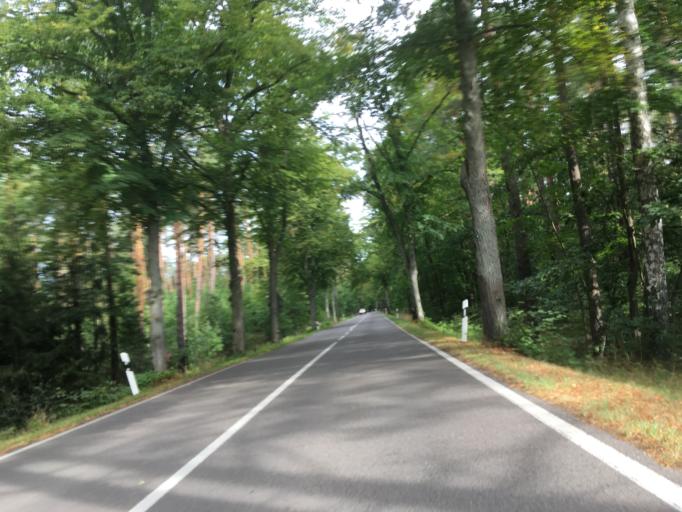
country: DE
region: Brandenburg
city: Templin
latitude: 53.1373
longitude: 13.5524
